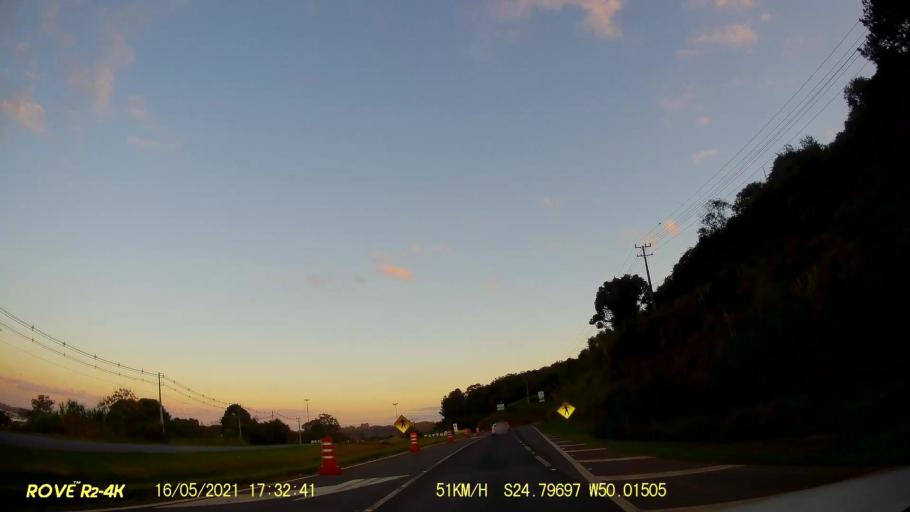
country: BR
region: Parana
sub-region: Castro
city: Castro
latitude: -24.7972
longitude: -50.0150
